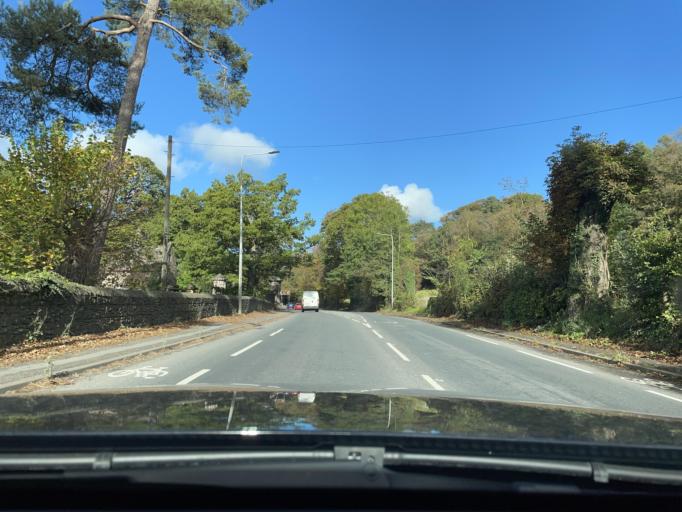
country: GB
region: England
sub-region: Cheshire East
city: Disley
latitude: 53.3565
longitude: -2.0529
